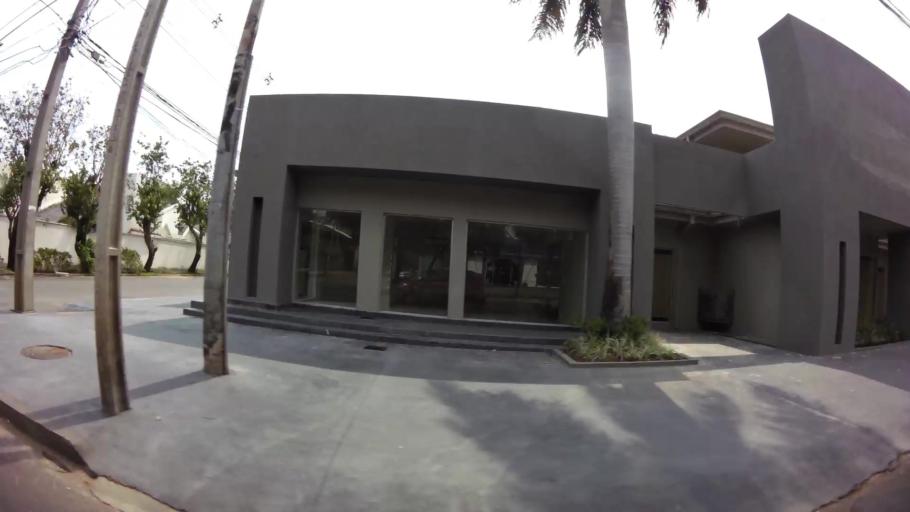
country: PY
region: Asuncion
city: Asuncion
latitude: -25.2830
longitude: -57.5714
